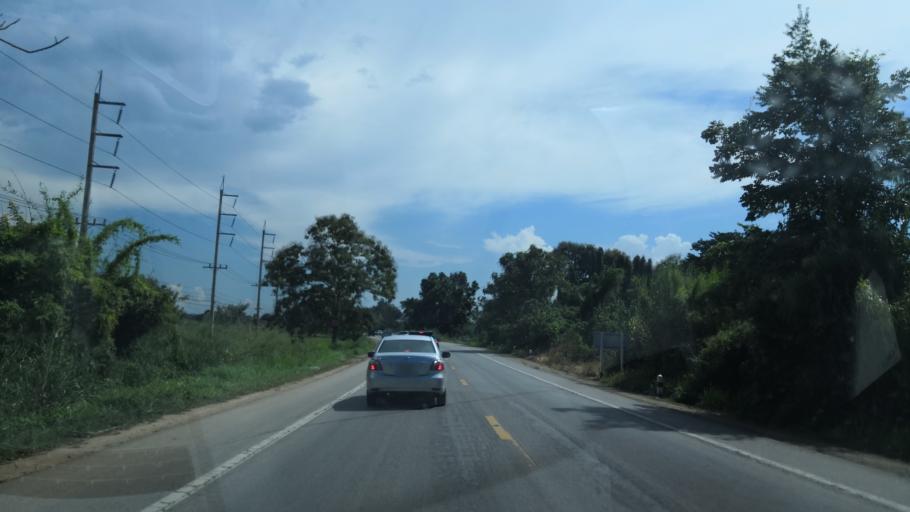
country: TH
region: Chiang Rai
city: Wiang Pa Pao
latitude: 19.4065
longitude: 99.5005
